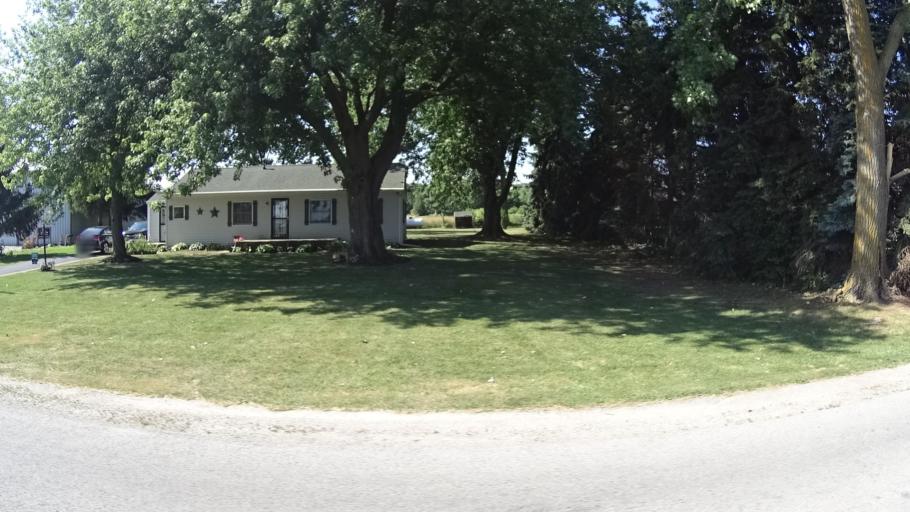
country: US
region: Ohio
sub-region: Huron County
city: Bellevue
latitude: 41.3747
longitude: -82.7931
